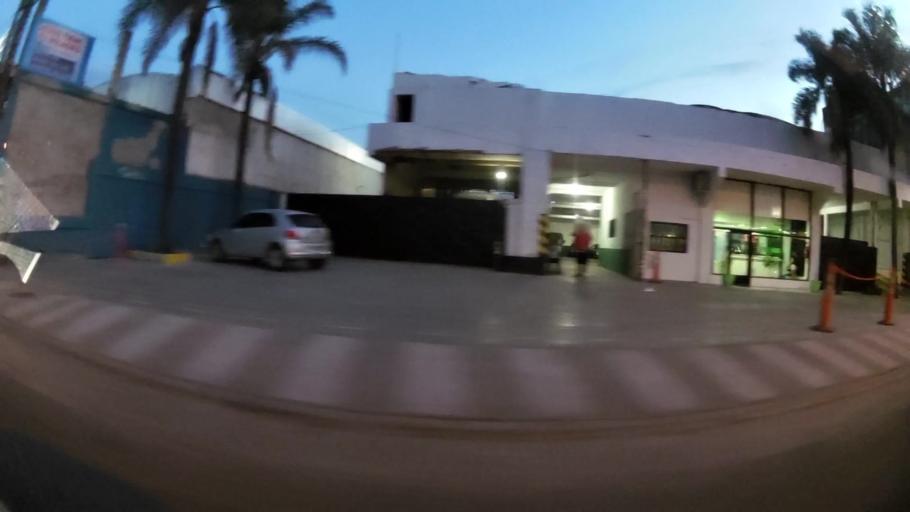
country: AR
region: Buenos Aires
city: Ituzaingo
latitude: -34.6596
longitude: -58.6652
